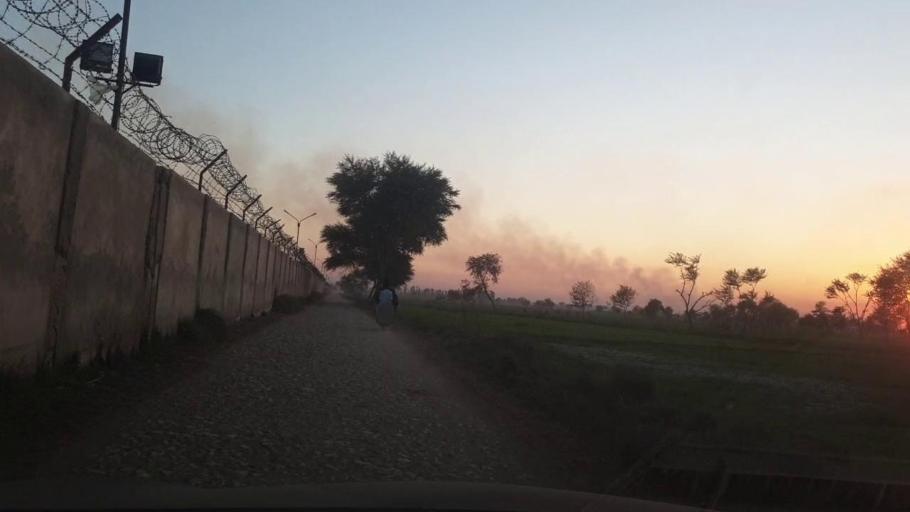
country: PK
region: Sindh
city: Ghotki
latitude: 28.0539
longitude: 69.3606
